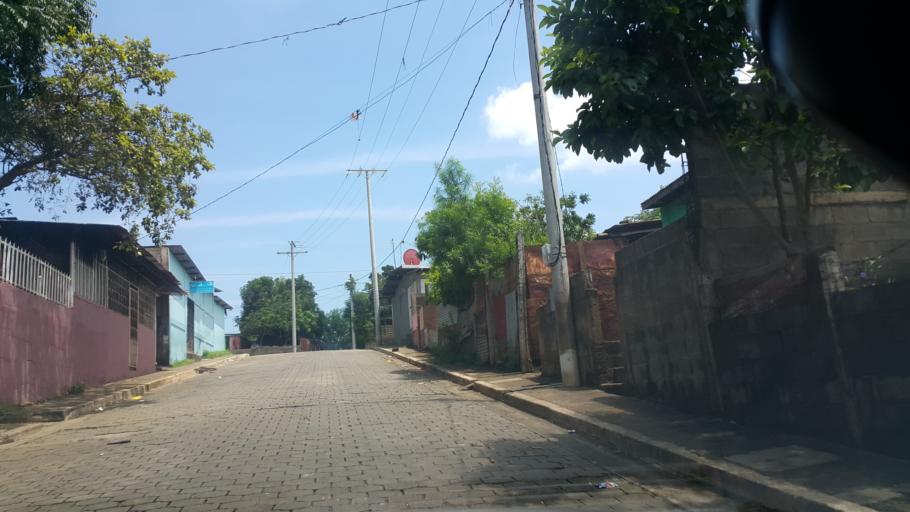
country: NI
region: Managua
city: Managua
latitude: 12.1068
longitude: -86.2408
